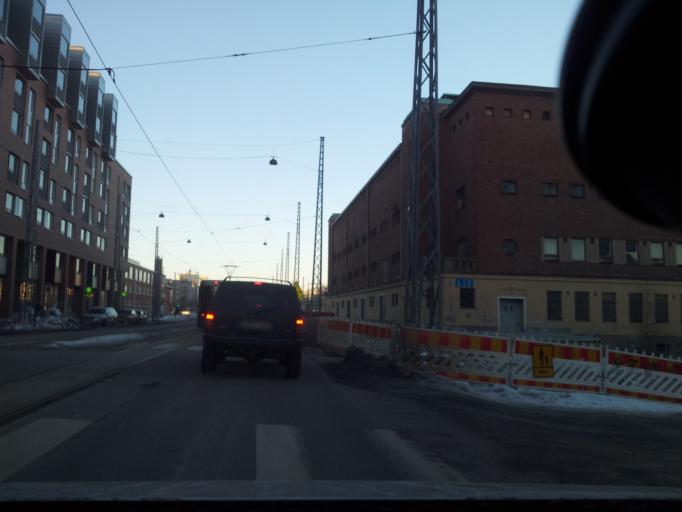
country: FI
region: Uusimaa
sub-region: Helsinki
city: Helsinki
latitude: 60.1582
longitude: 24.9217
